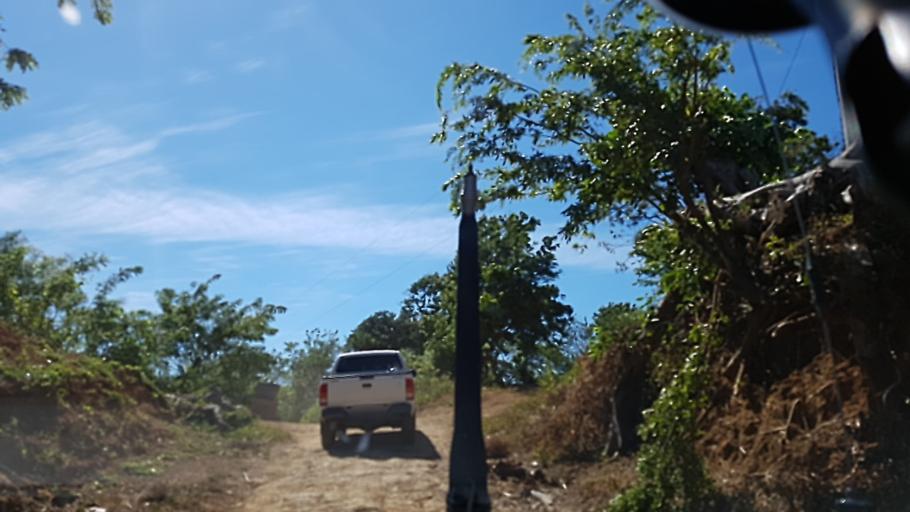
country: NI
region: Carazo
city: Santa Teresa
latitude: 11.6726
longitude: -86.1785
